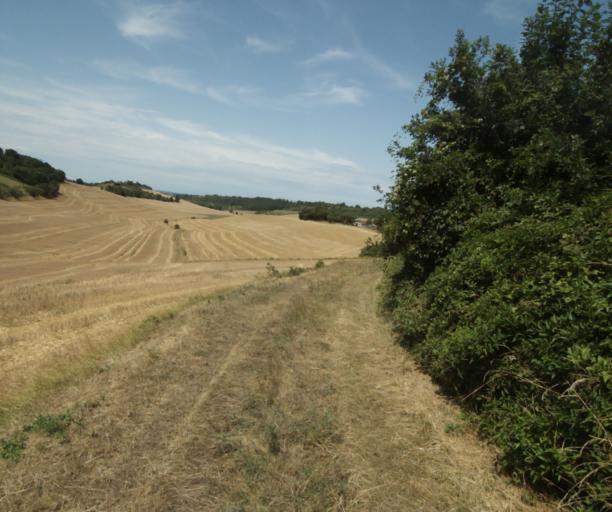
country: FR
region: Midi-Pyrenees
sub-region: Departement de la Haute-Garonne
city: Saint-Felix-Lauragais
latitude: 43.4439
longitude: 1.8811
